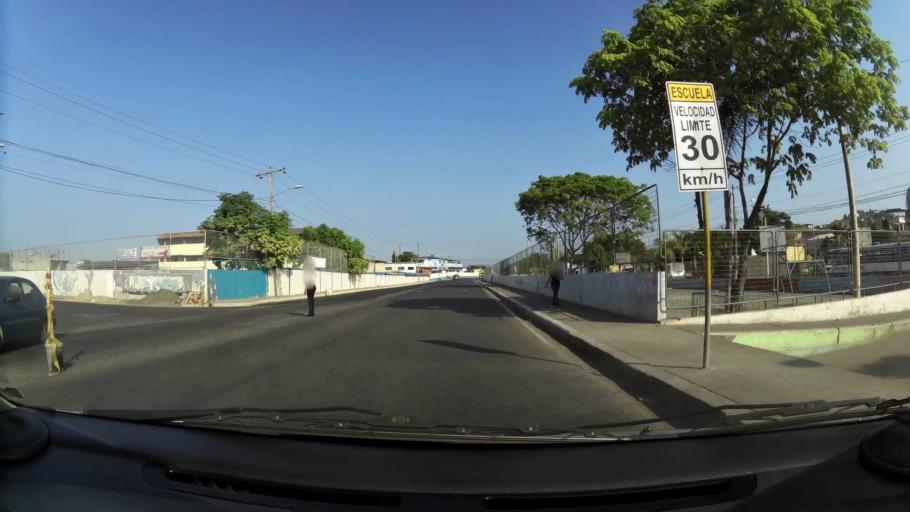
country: EC
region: Guayas
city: Eloy Alfaro
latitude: -2.1797
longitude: -79.8475
